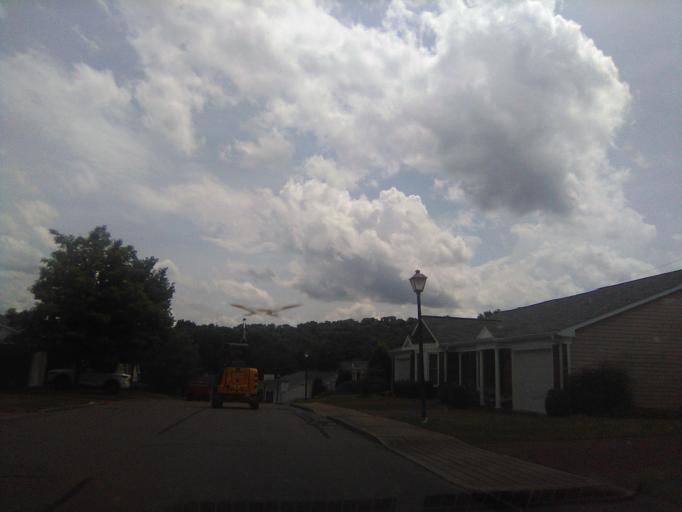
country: US
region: Tennessee
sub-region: Davidson County
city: Belle Meade
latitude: 36.0884
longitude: -86.8896
